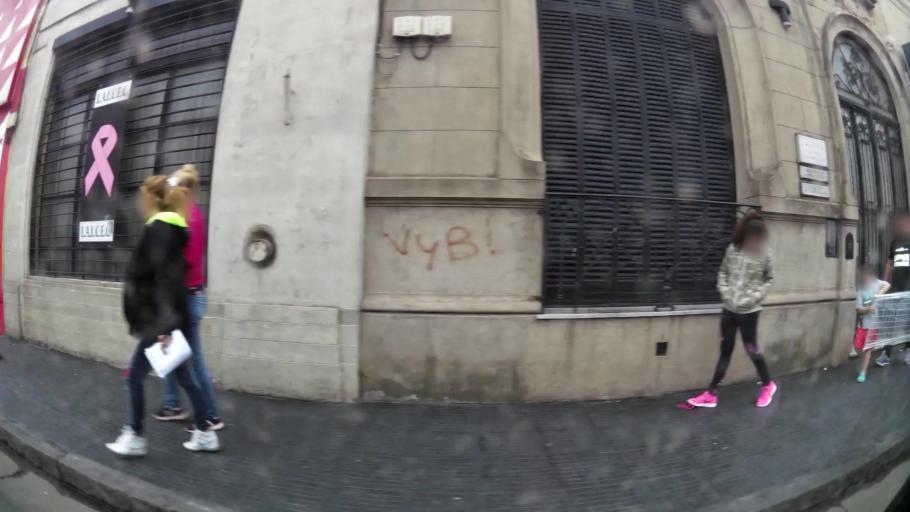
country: AR
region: Buenos Aires
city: San Nicolas de los Arroyos
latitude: -33.3332
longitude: -60.2215
